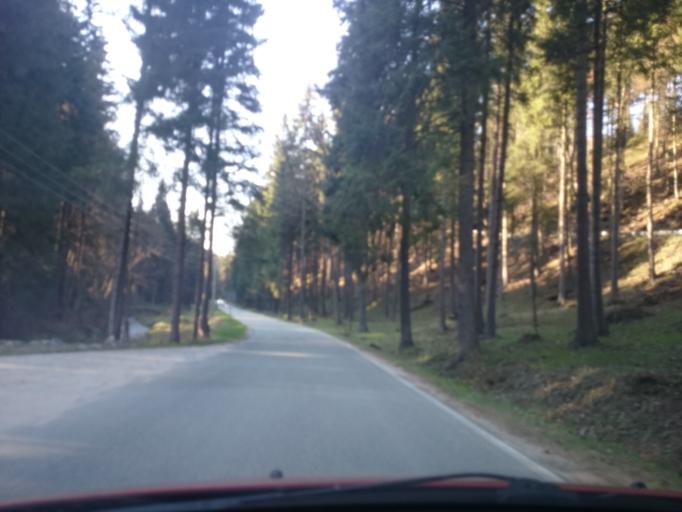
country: PL
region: Lower Silesian Voivodeship
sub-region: Powiat klodzki
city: Duszniki-Zdroj
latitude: 50.3474
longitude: 16.4006
